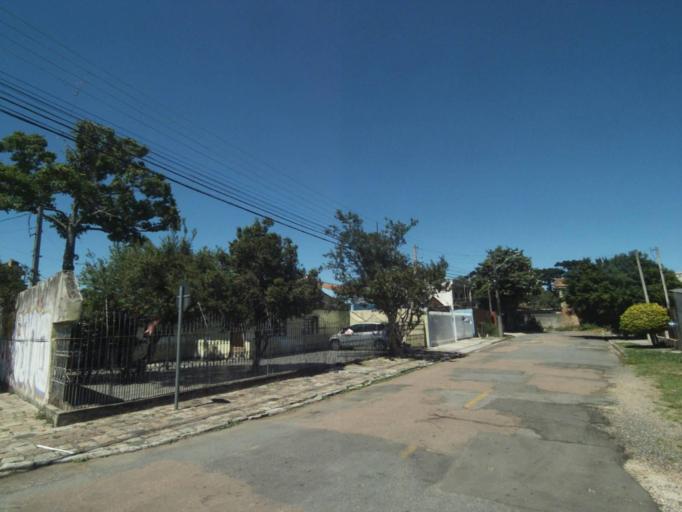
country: BR
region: Parana
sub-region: Curitiba
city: Curitiba
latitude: -25.4756
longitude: -49.3445
